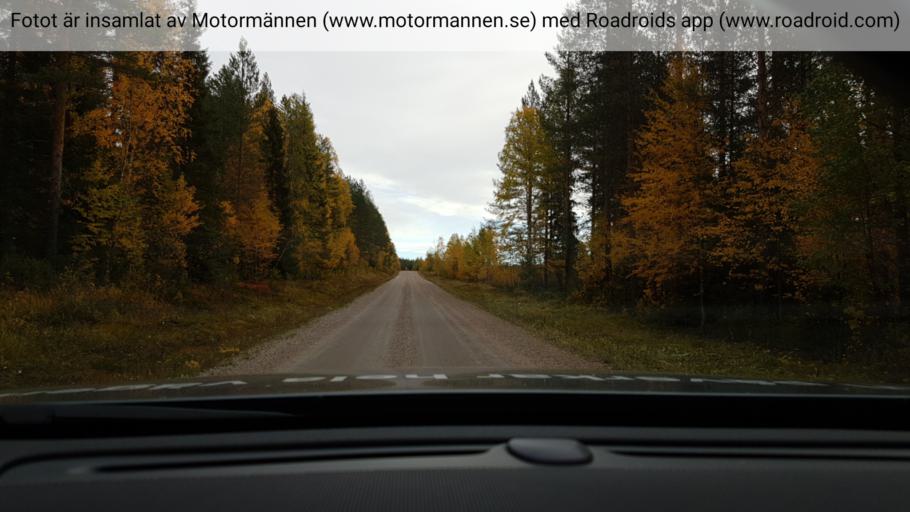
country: SE
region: Norrbotten
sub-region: Overkalix Kommun
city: OEverkalix
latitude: 66.2677
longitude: 23.0077
